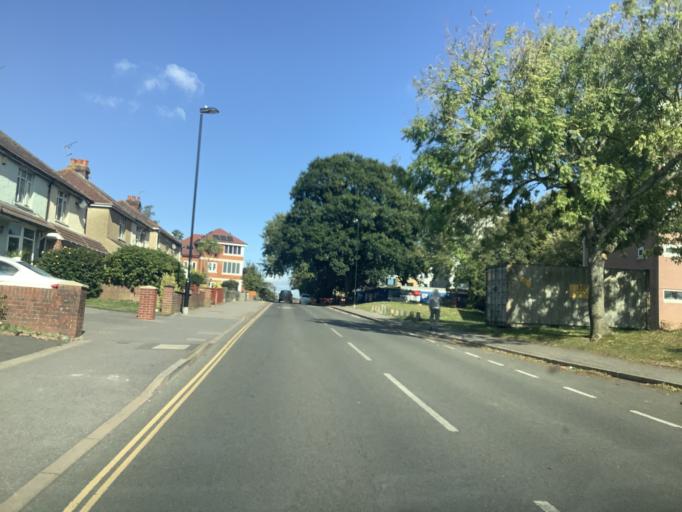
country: GB
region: England
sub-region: Hampshire
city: Marchwood
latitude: 50.9290
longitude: -1.4497
